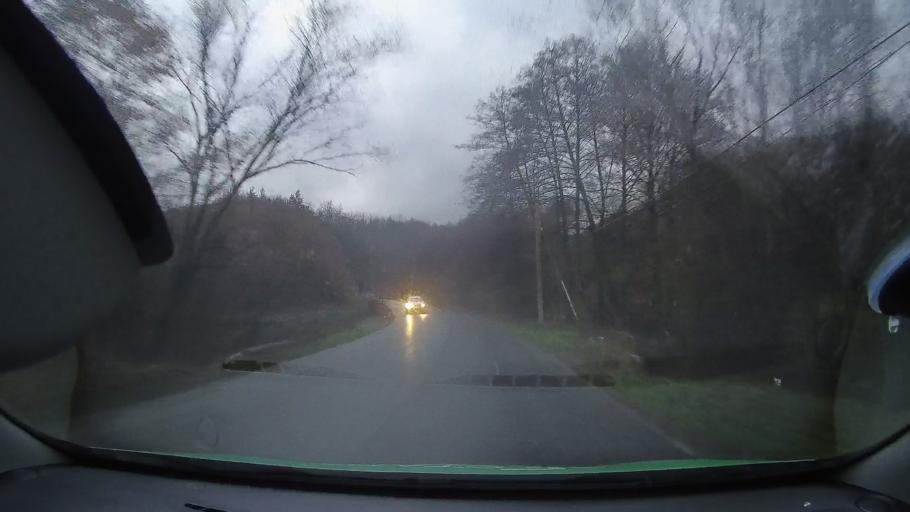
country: RO
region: Hunedoara
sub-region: Comuna Baia de Cris
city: Baia de Cris
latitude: 46.1975
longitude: 22.7172
